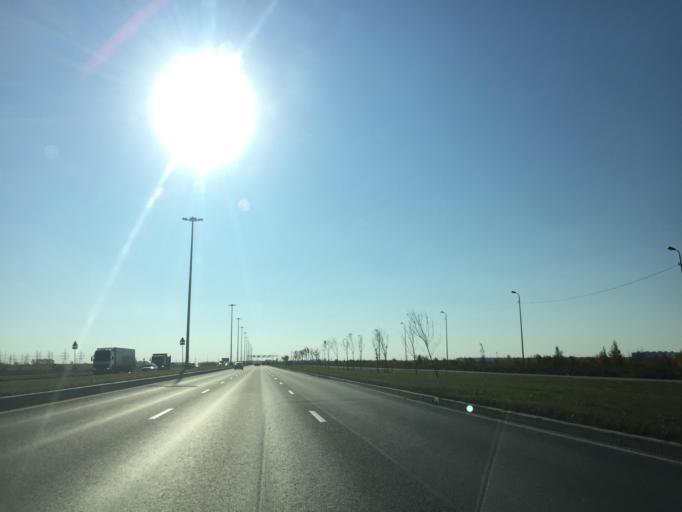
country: RU
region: St.-Petersburg
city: Petro-Slavyanka
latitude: 59.7763
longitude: 30.4985
